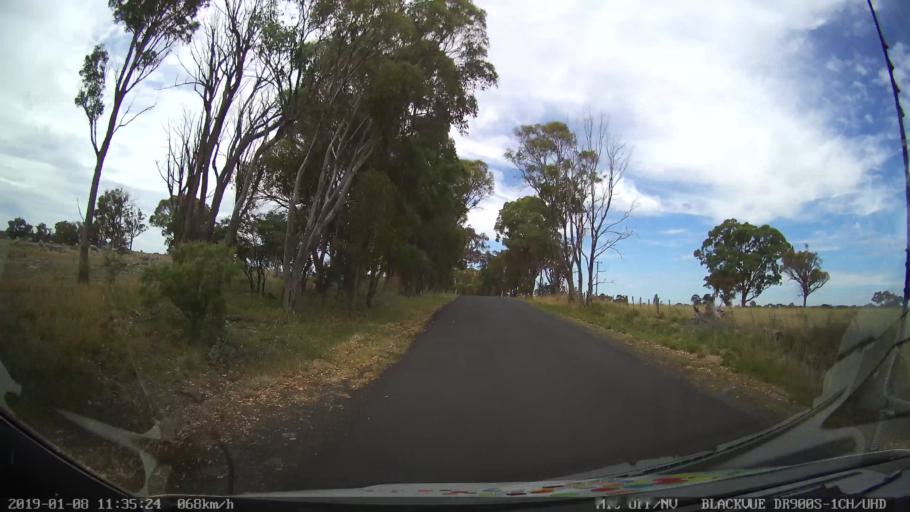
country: AU
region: New South Wales
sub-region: Guyra
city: Guyra
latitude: -30.3368
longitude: 151.5378
